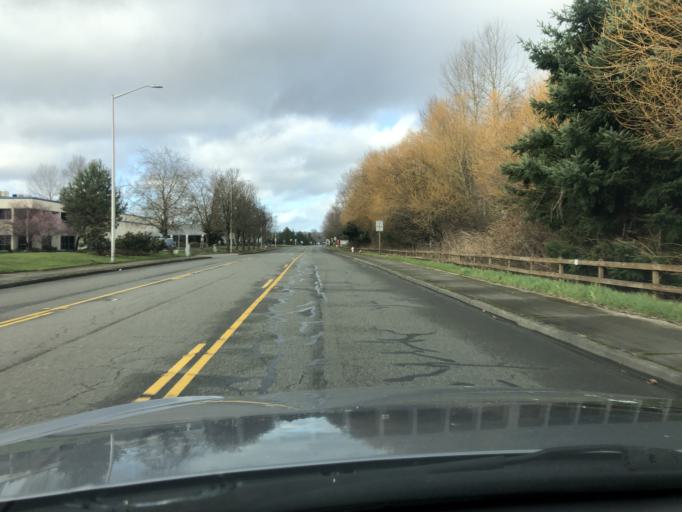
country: US
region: Washington
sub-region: King County
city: Tukwila
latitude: 47.4289
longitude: -122.2441
